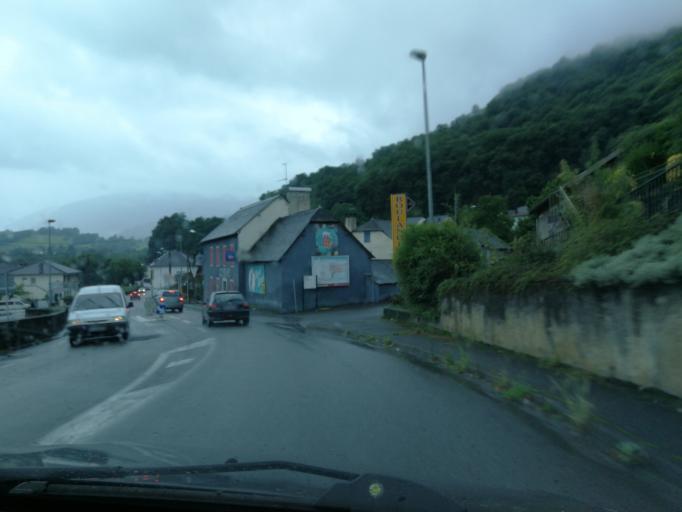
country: FR
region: Aquitaine
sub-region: Departement des Pyrenees-Atlantiques
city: Oloron-Sainte-Marie
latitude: 43.1229
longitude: -0.6135
